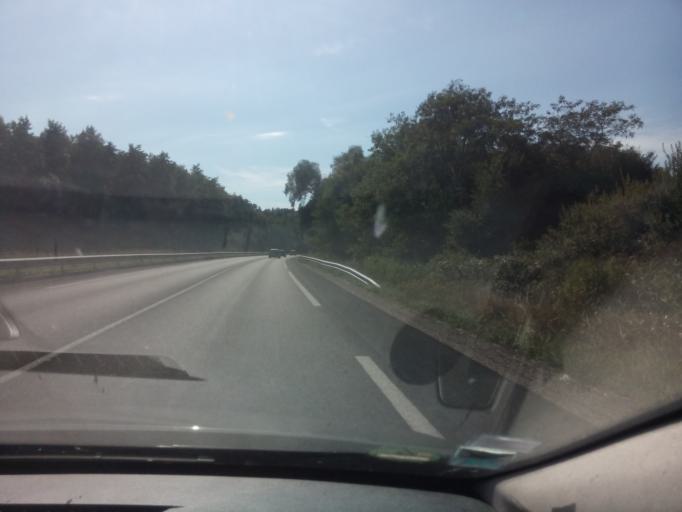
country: FR
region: Alsace
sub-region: Departement du Bas-Rhin
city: Surbourg
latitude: 48.8973
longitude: 7.8475
